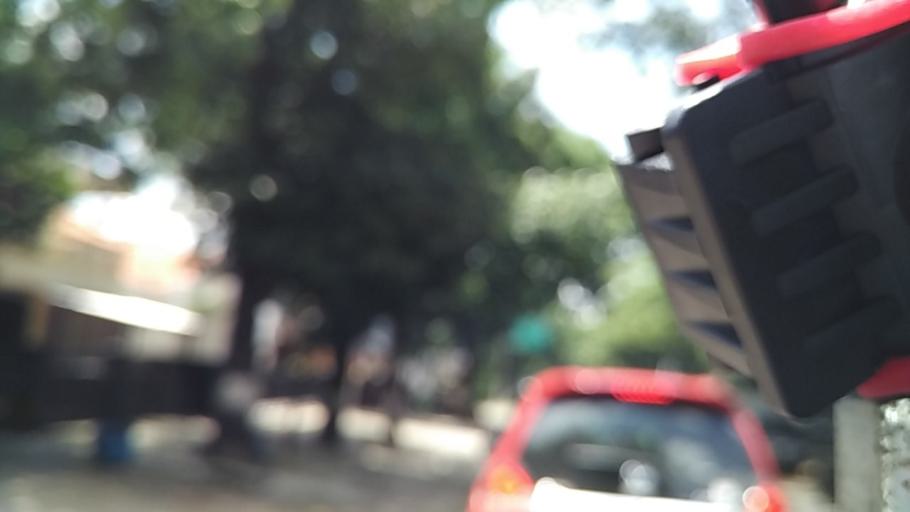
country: ID
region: Central Java
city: Semarang
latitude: -7.0060
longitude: 110.3795
